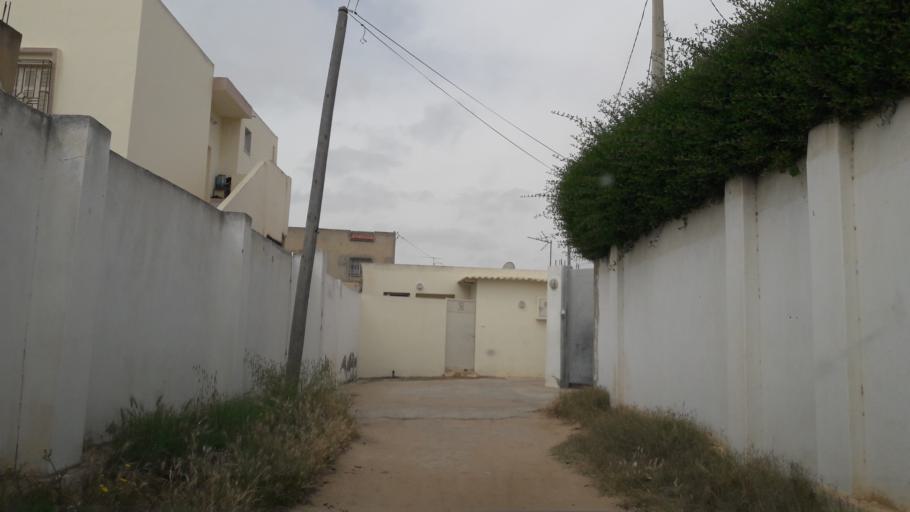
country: TN
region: Safaqis
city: Al Qarmadah
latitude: 34.7937
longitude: 10.7573
